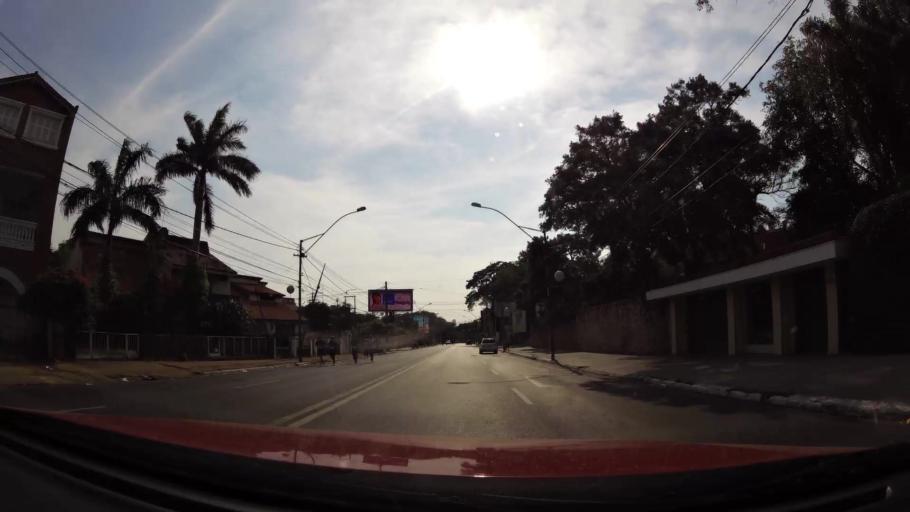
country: PY
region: Asuncion
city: Asuncion
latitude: -25.2916
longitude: -57.5986
